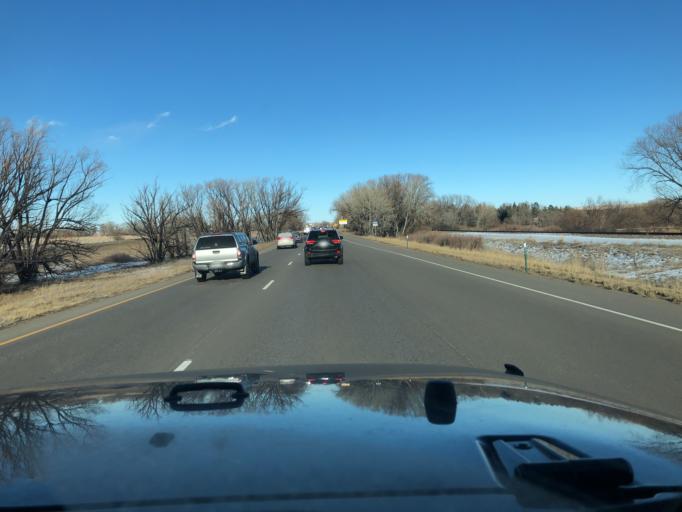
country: US
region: Colorado
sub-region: Boulder County
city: Boulder
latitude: 40.0536
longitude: -105.2298
